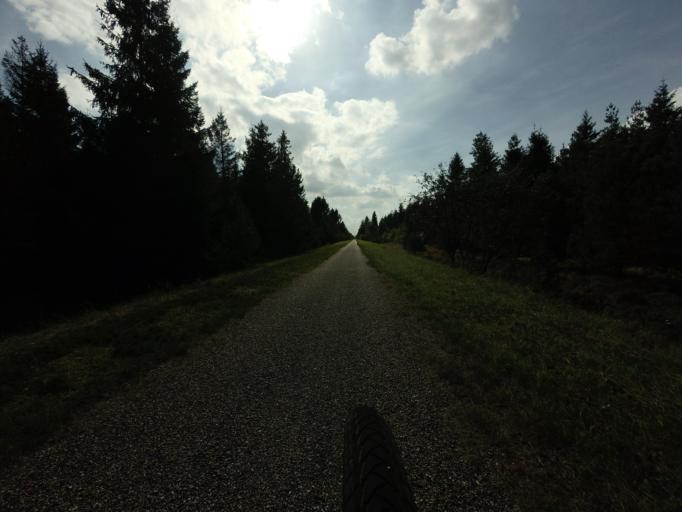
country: DK
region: Central Jutland
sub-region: Viborg Kommune
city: Karup
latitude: 56.2538
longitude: 9.1048
